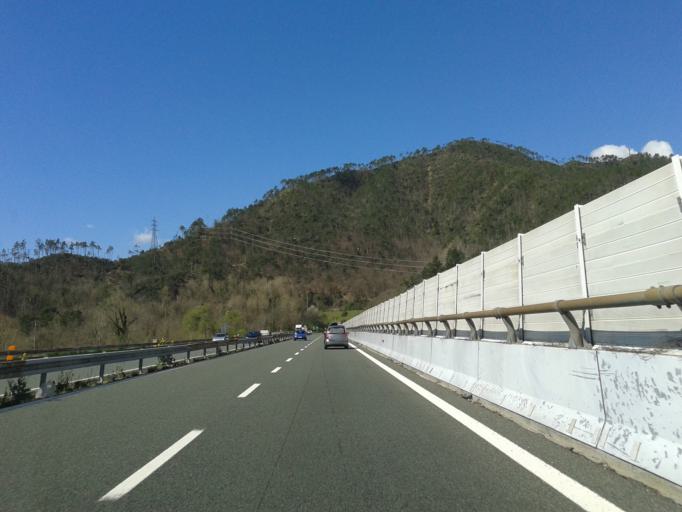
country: IT
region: Liguria
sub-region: Provincia di La Spezia
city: Beverino
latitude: 44.2057
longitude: 9.7880
